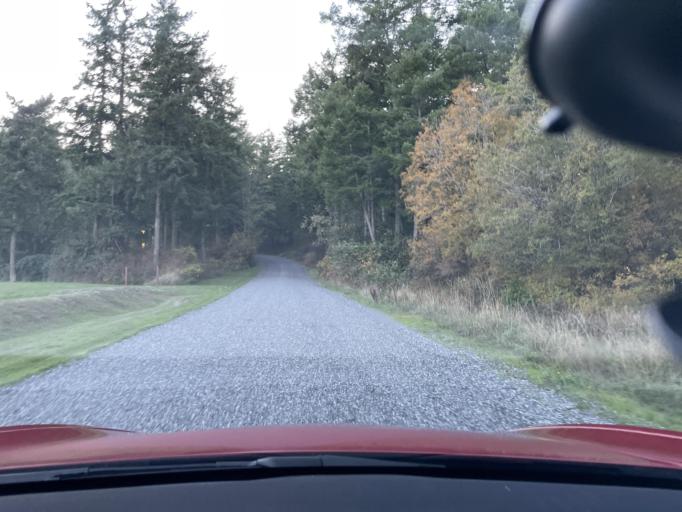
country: US
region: Washington
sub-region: San Juan County
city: Friday Harbor
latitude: 48.6138
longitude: -123.1458
